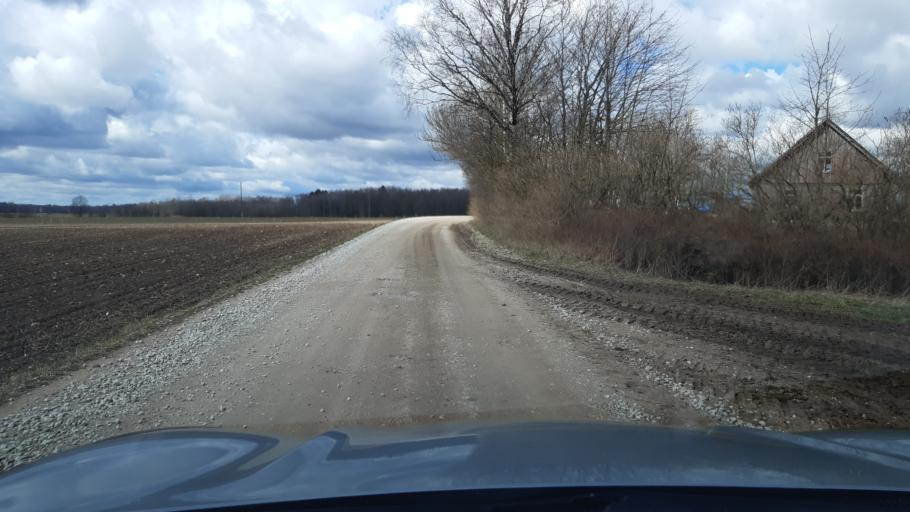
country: EE
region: Raplamaa
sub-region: Kehtna vald
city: Kehtna
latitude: 59.0613
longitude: 25.1021
